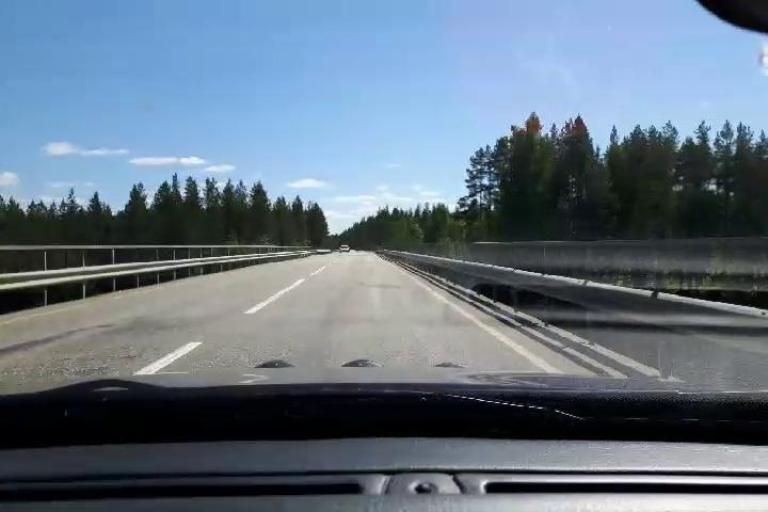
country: SE
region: Jaemtland
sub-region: Harjedalens Kommun
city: Sveg
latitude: 62.1225
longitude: 15.0360
